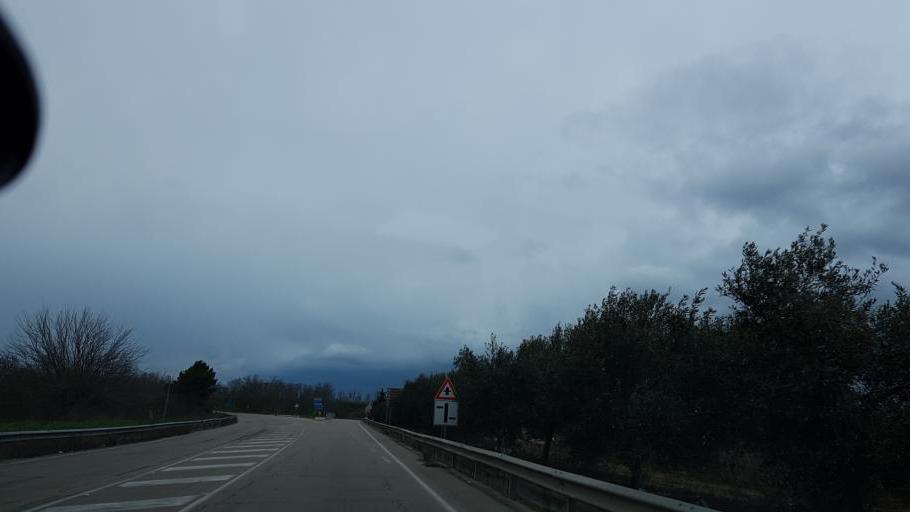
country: IT
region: Apulia
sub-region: Provincia di Brindisi
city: La Rosa
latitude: 40.6144
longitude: 17.9521
